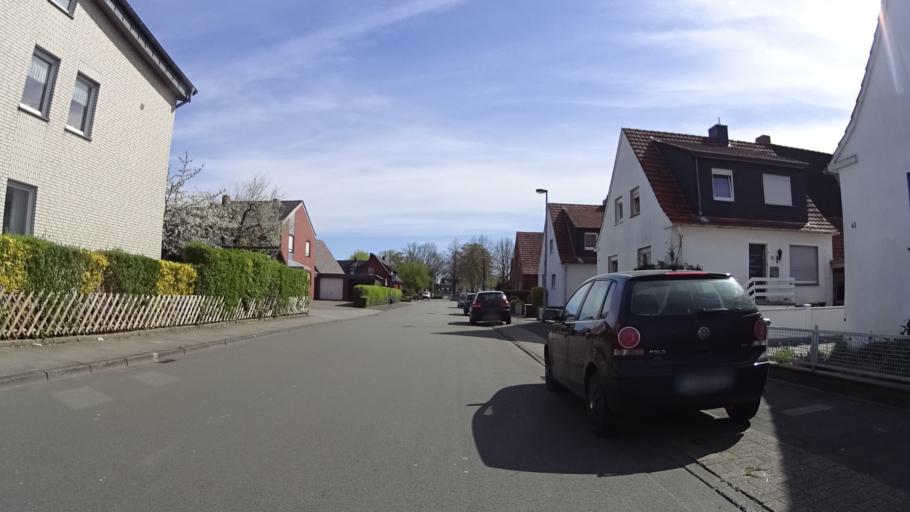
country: DE
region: North Rhine-Westphalia
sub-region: Regierungsbezirk Munster
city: Dreierwalde
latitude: 52.2890
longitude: 7.4731
